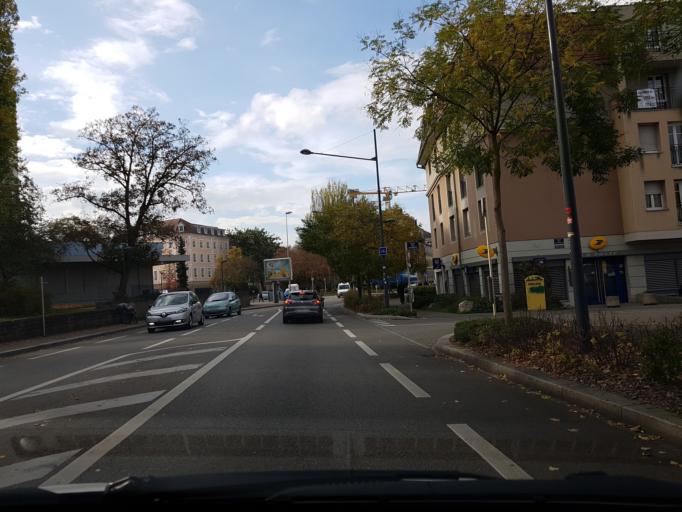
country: FR
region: Alsace
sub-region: Departement du Haut-Rhin
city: Mulhouse
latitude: 47.7440
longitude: 7.3332
